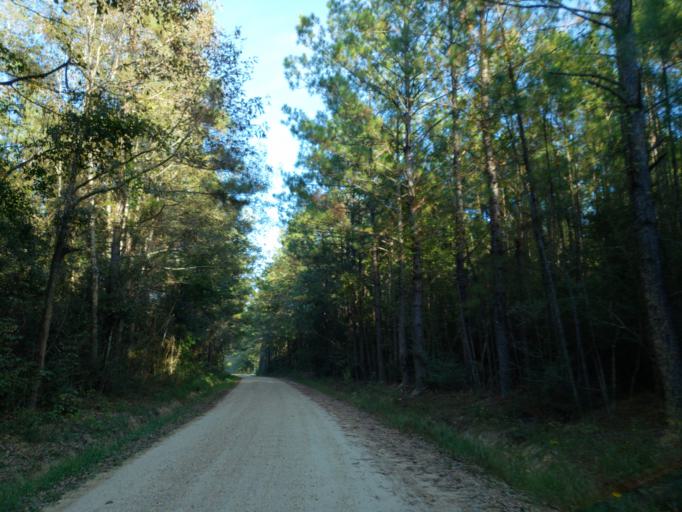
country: US
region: Mississippi
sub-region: Perry County
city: Richton
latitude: 31.3524
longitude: -88.8086
